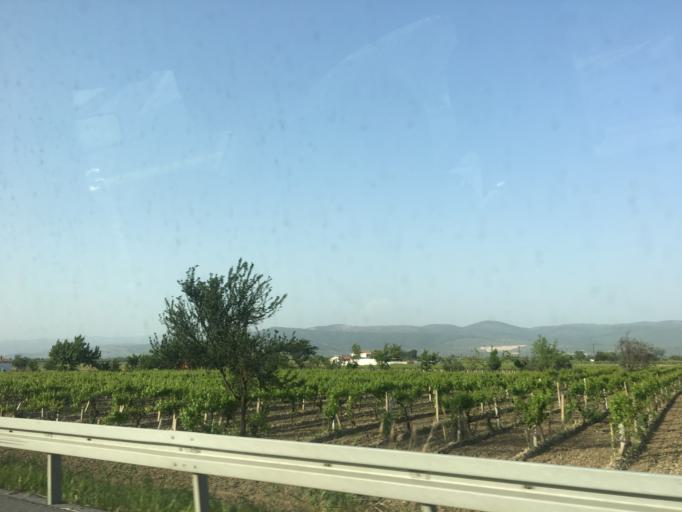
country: TR
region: Manisa
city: Golmarmara
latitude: 38.6817
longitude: 27.9428
